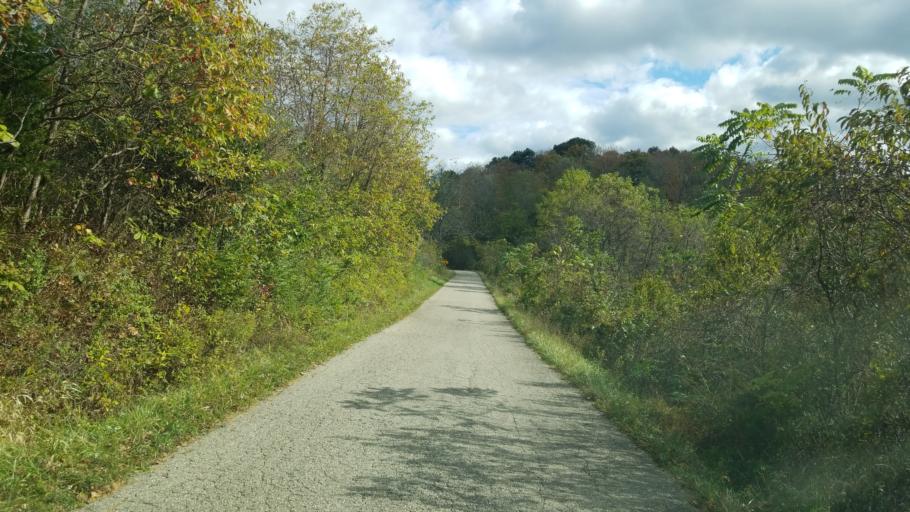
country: US
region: Ohio
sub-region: Jackson County
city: Jackson
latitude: 39.0907
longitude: -82.5872
